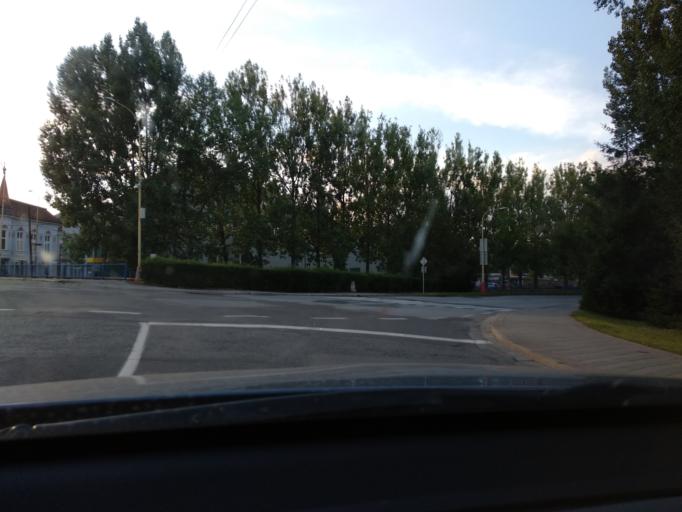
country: SK
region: Zilinsky
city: Ruzomberok
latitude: 49.0790
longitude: 19.3060
